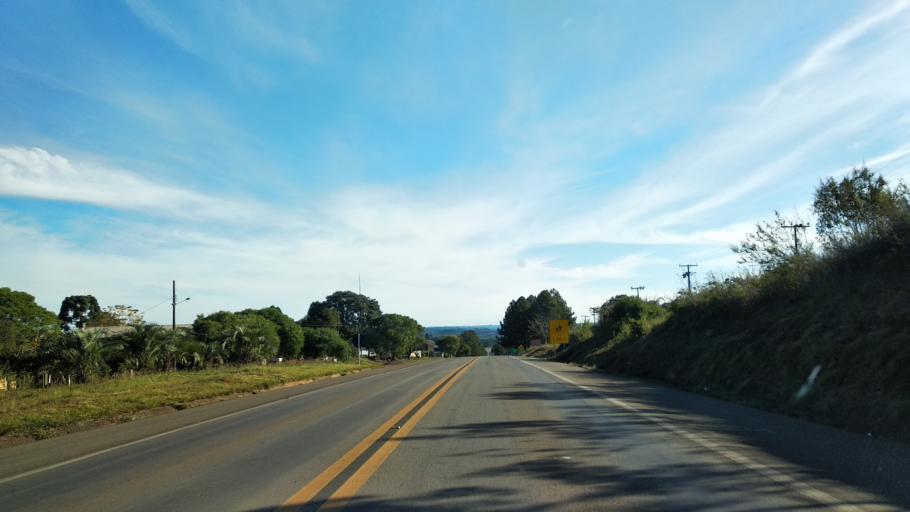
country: BR
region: Santa Catarina
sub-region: Celso Ramos
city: Celso Ramos
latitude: -27.5288
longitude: -51.3840
